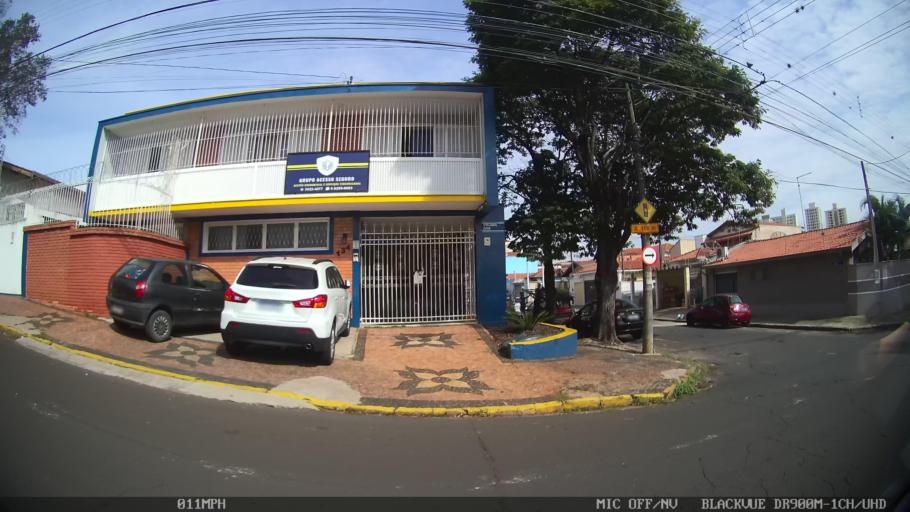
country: BR
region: Sao Paulo
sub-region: Piracicaba
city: Piracicaba
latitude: -22.7401
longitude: -47.6514
